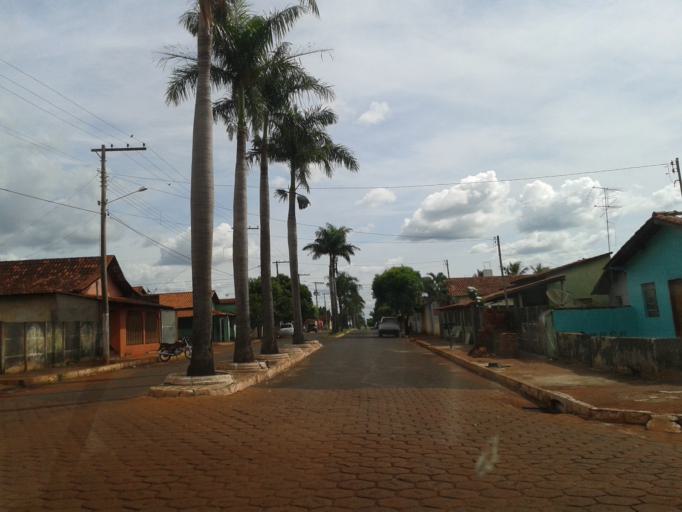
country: BR
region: Minas Gerais
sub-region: Centralina
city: Centralina
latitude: -18.5900
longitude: -49.1979
